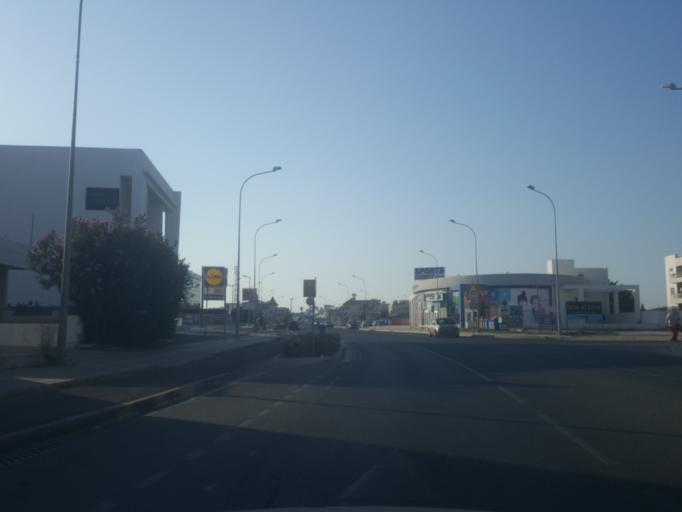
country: CY
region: Ammochostos
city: Paralimni
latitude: 35.0488
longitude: 33.9774
